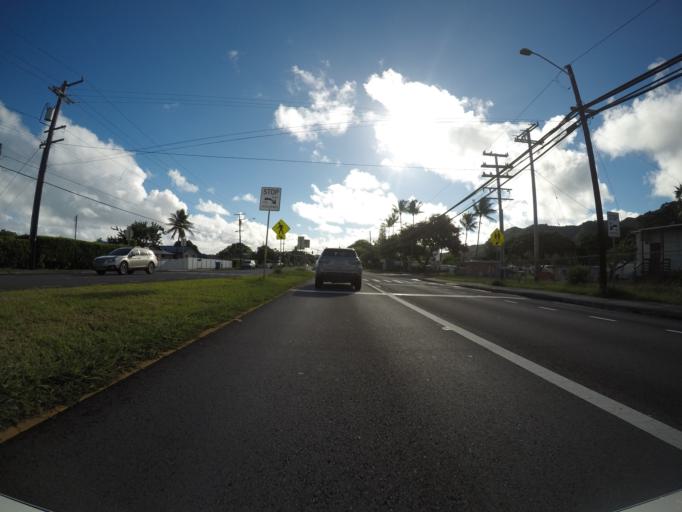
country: US
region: Hawaii
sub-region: Honolulu County
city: Kane'ohe
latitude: 21.4045
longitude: -157.7952
